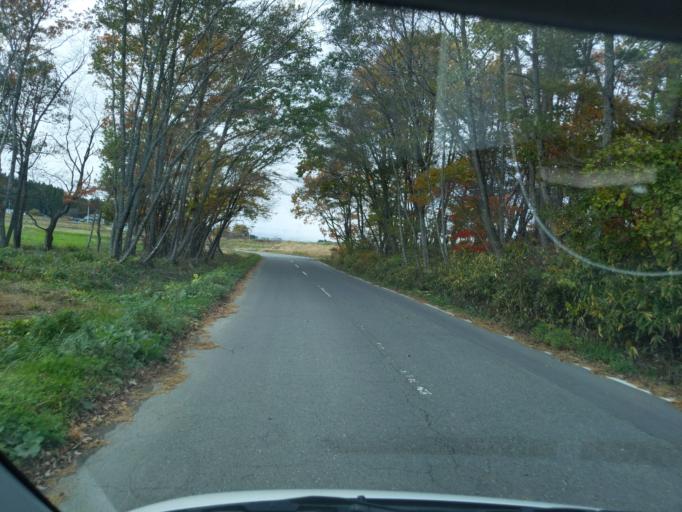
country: JP
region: Iwate
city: Mizusawa
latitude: 39.0467
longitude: 141.0754
